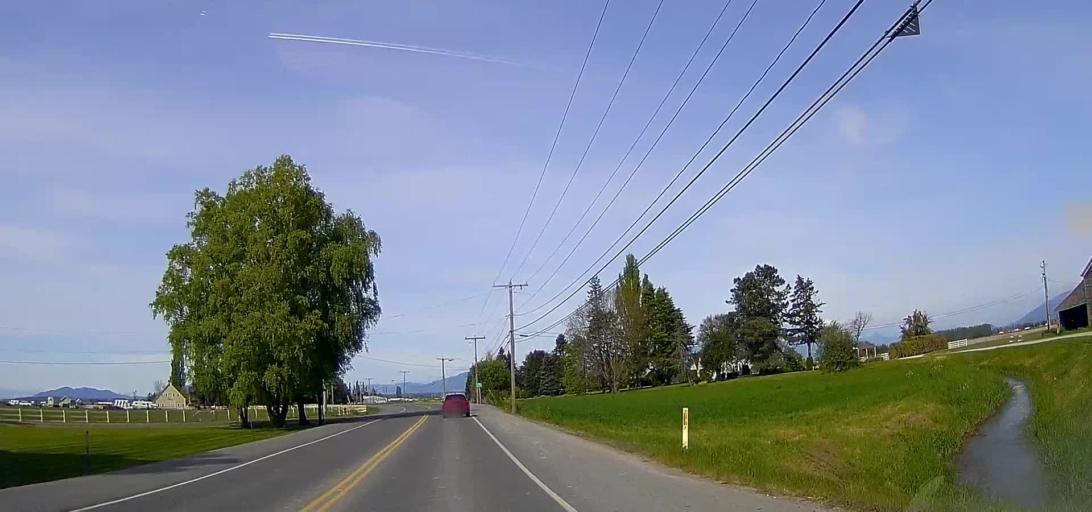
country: US
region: Washington
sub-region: Skagit County
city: Mount Vernon
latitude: 48.4065
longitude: -122.4743
